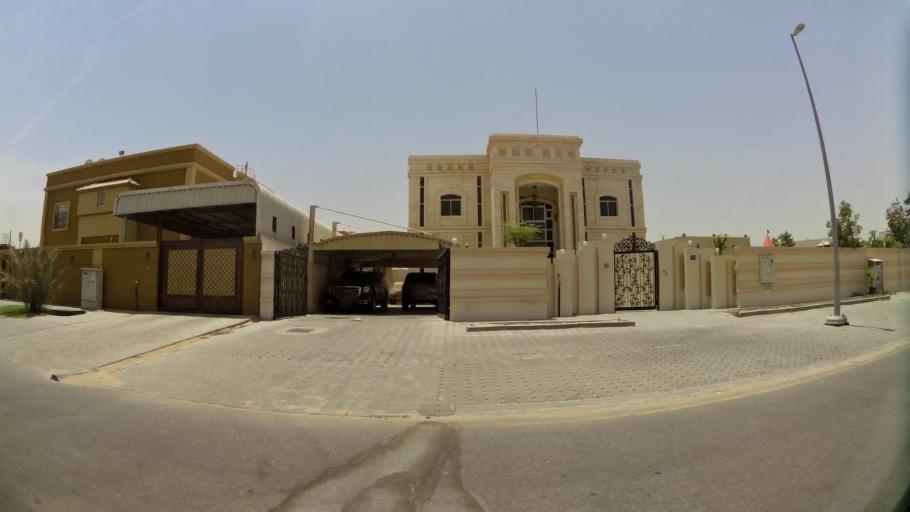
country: AE
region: Ash Shariqah
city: Sharjah
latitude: 25.2529
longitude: 55.4650
